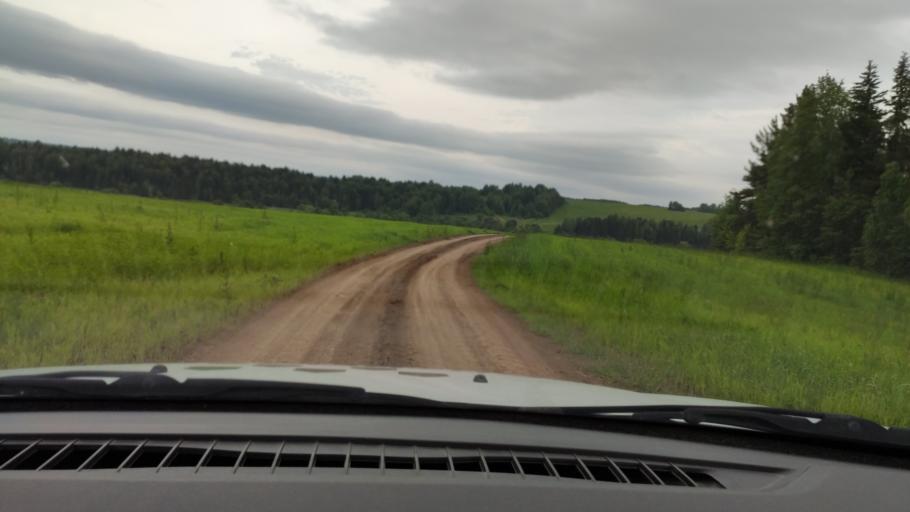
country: RU
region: Perm
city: Orda
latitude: 57.2960
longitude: 56.5944
